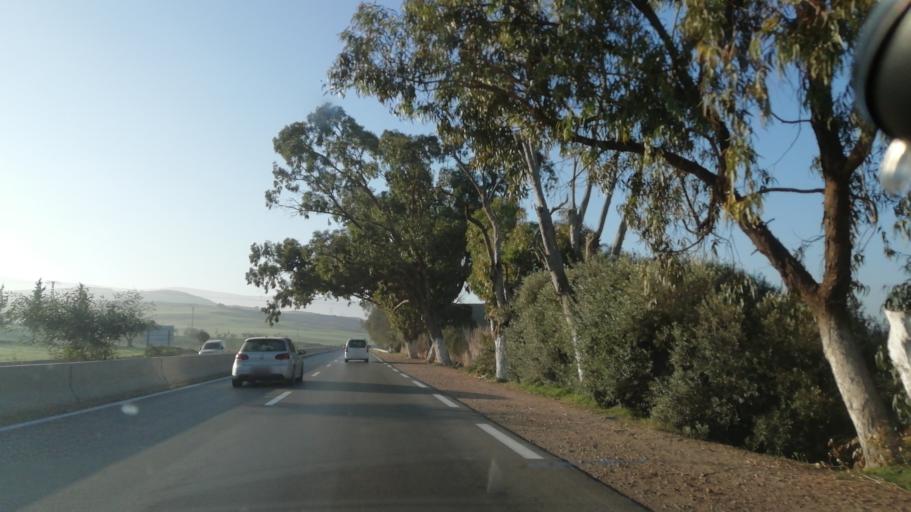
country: DZ
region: Ain Temouchent
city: Beni Saf
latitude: 35.2028
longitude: -1.4198
